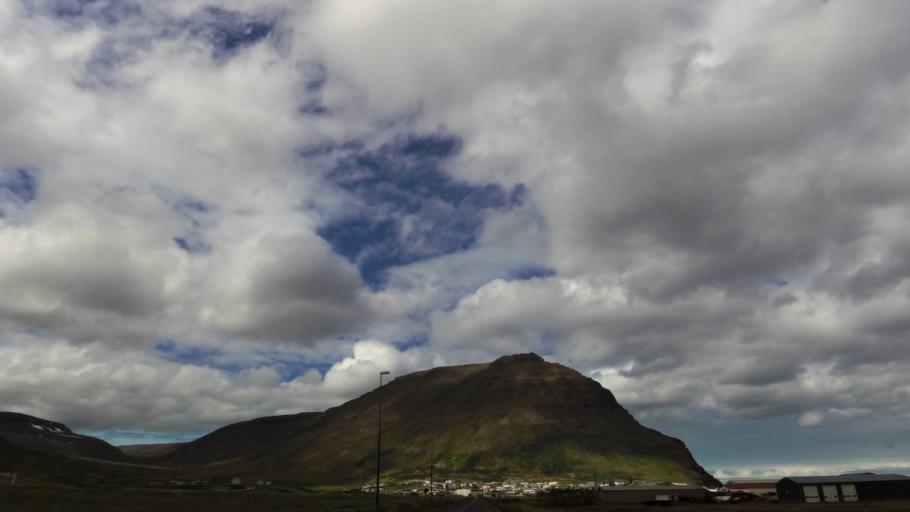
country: IS
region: Westfjords
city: Isafjoerdur
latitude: 66.1492
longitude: -23.2435
